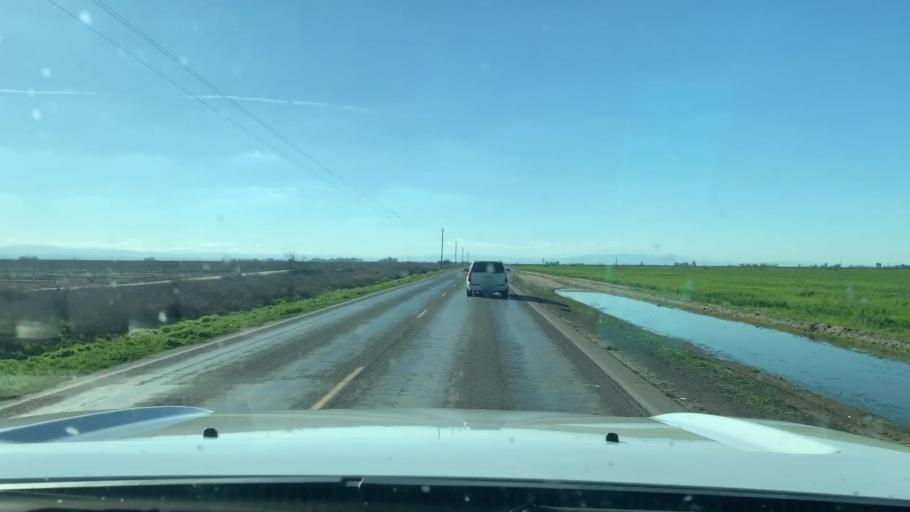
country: US
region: California
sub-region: Kings County
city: Stratford
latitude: 36.2111
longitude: -119.7290
